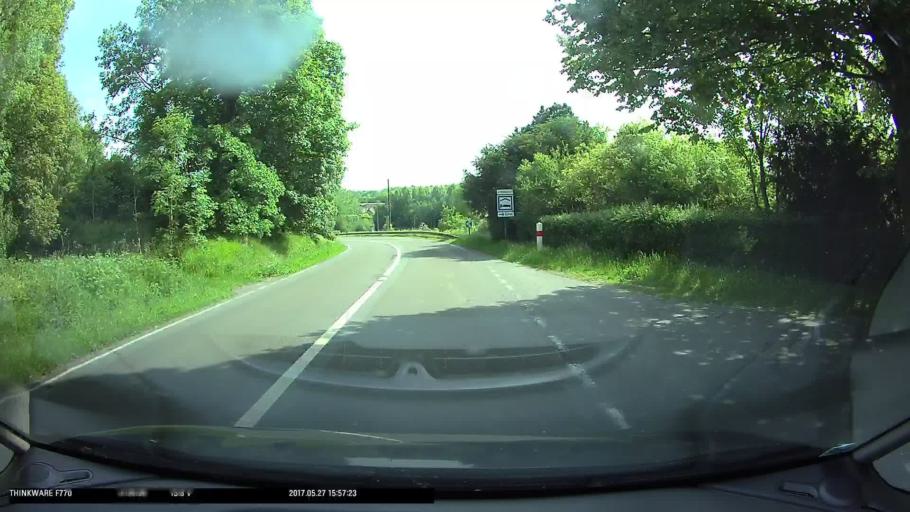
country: FR
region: Ile-de-France
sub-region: Departement du Val-d'Oise
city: Us
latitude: 49.1045
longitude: 1.9712
